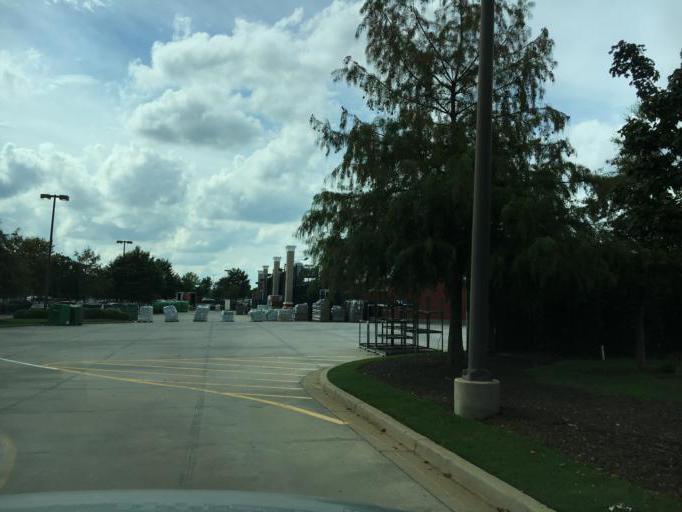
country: US
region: South Carolina
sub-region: Greenville County
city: Mauldin
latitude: 34.8261
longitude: -82.2952
